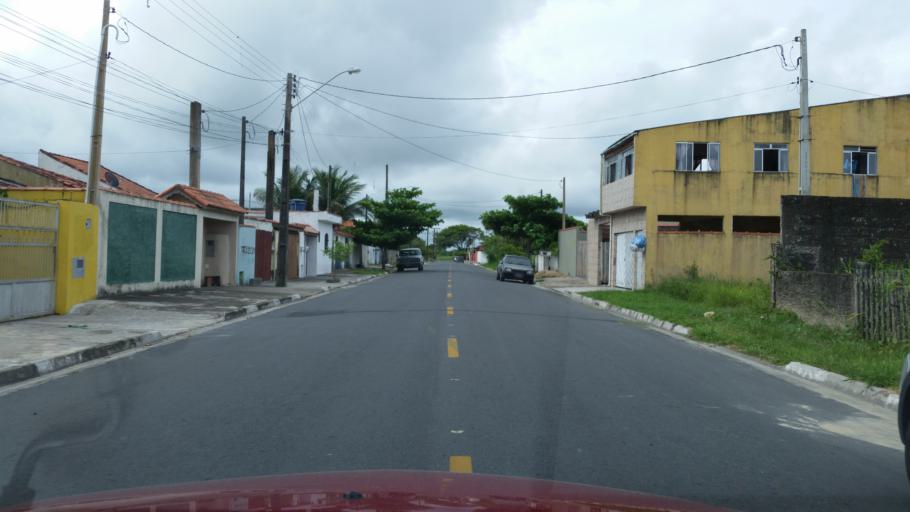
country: BR
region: Sao Paulo
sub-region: Iguape
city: Iguape
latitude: -24.7427
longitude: -47.5552
